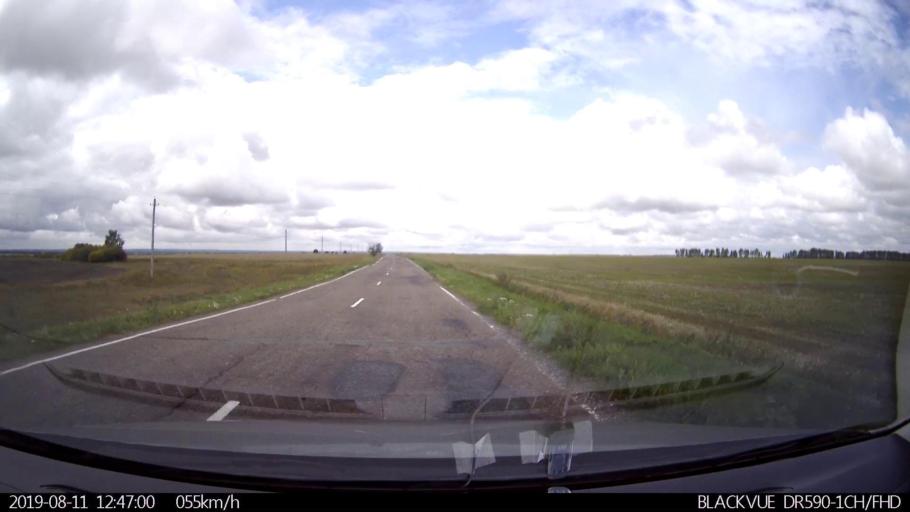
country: RU
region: Ulyanovsk
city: Ignatovka
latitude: 53.8673
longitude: 47.7130
